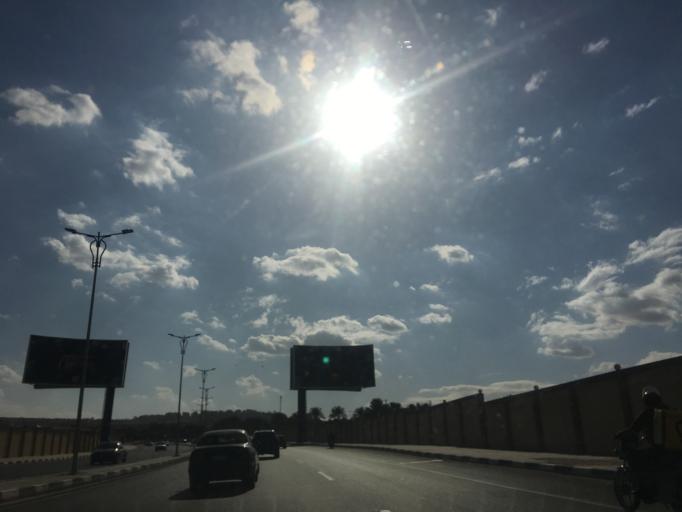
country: EG
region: Muhafazat al Qahirah
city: Cairo
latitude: 30.0391
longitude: 31.3068
